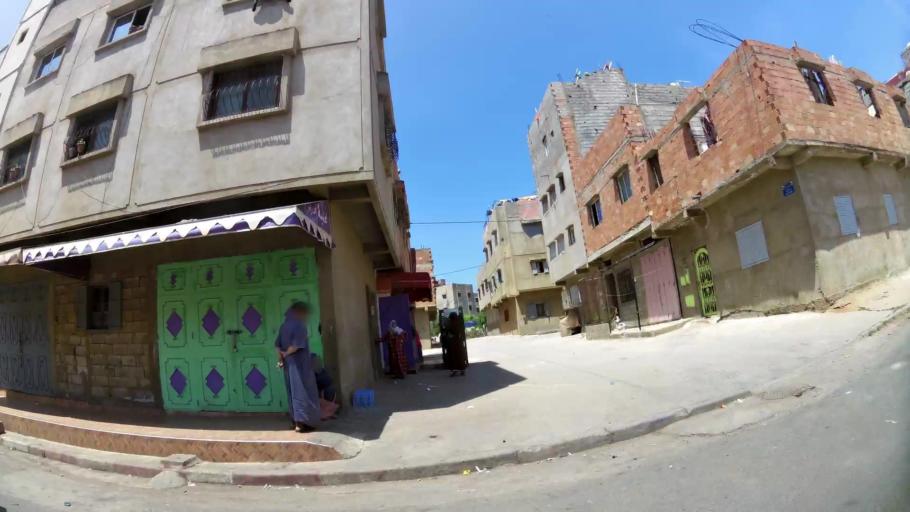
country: MA
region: Rabat-Sale-Zemmour-Zaer
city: Sale
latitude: 34.0695
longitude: -6.7823
